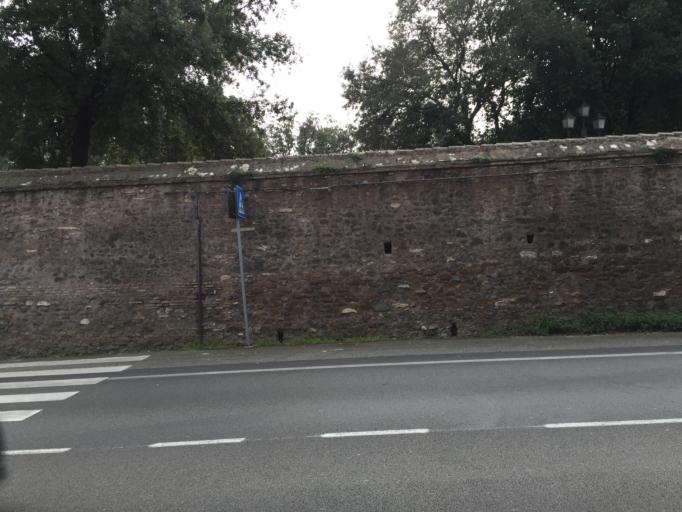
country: VA
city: Vatican City
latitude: 41.8890
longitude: 12.4522
